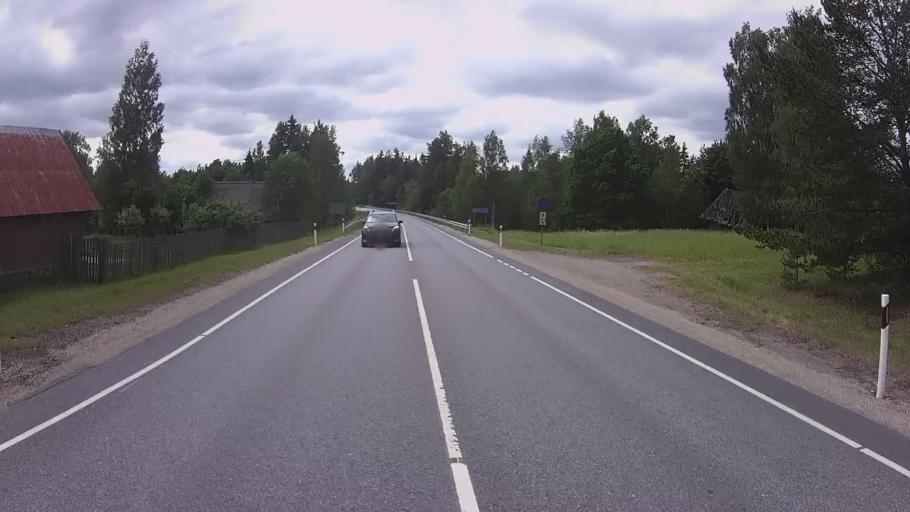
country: EE
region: Polvamaa
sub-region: Polva linn
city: Polva
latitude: 58.1239
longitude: 26.9553
